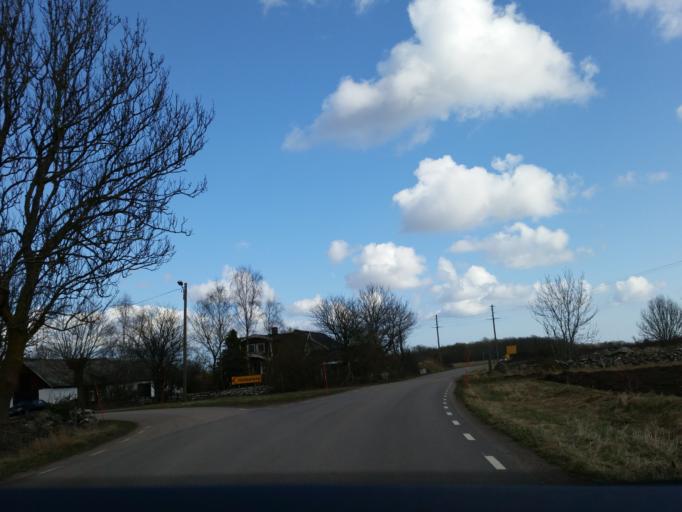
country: SE
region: Kalmar
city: Faerjestaden
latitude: 56.6888
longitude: 16.5611
